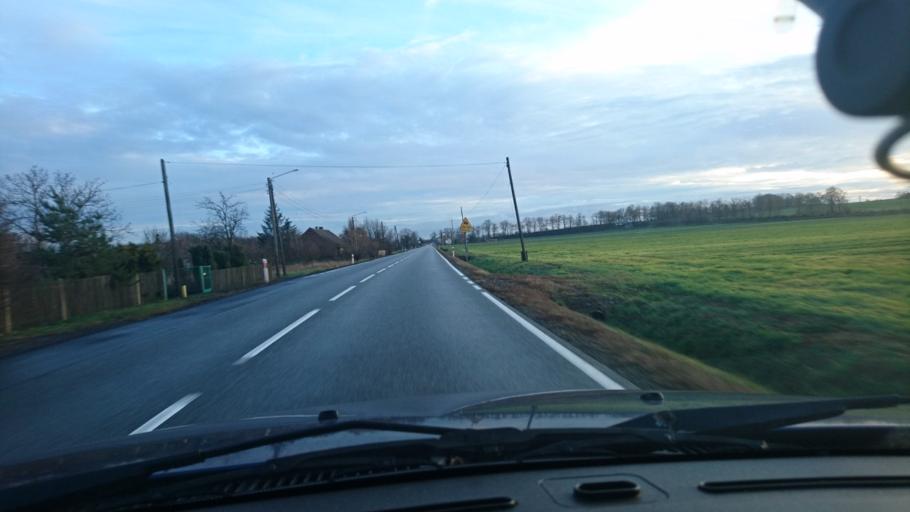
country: PL
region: Opole Voivodeship
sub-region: Powiat kluczborski
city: Byczyna
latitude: 51.1420
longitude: 18.1943
